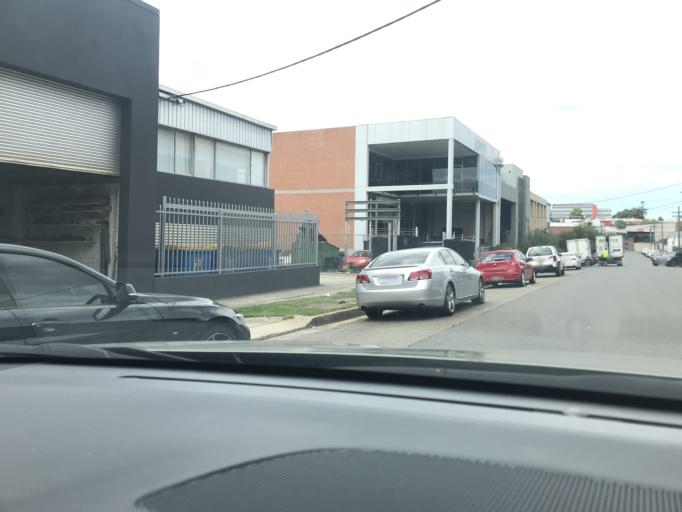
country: AU
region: New South Wales
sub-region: Ashfield
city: Croydon
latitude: -33.8697
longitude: 151.1163
